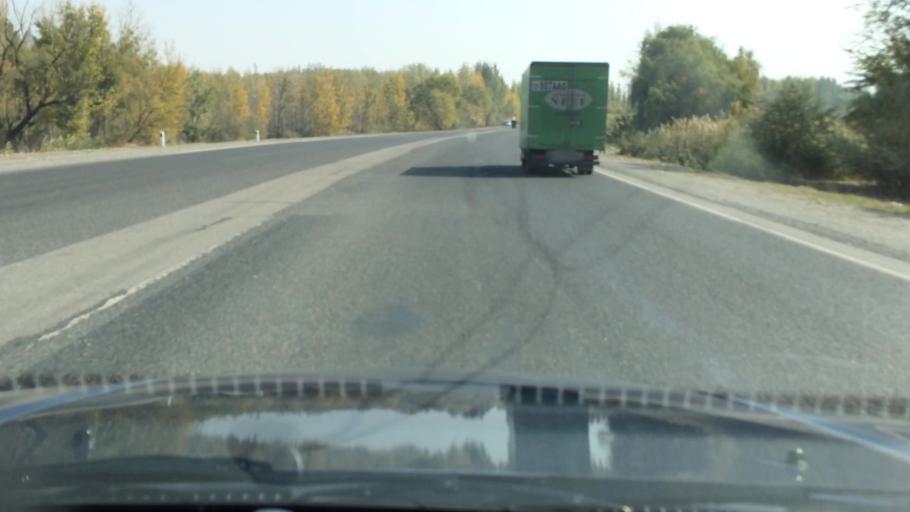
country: KG
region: Chuy
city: Ivanovka
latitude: 42.9392
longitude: 74.9789
